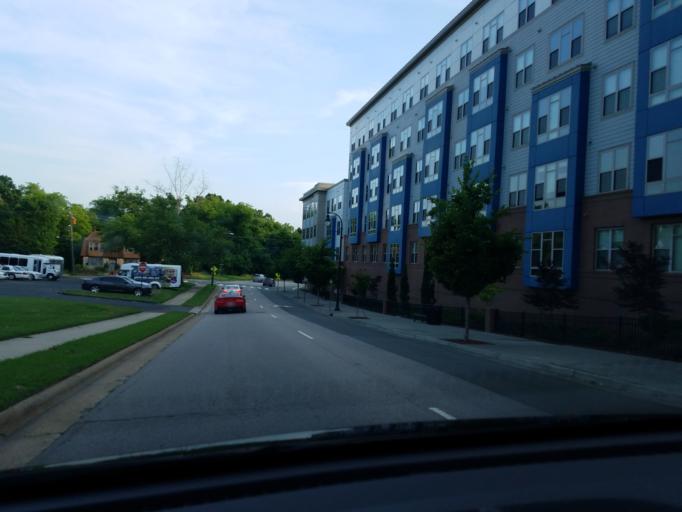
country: US
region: North Carolina
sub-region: Durham County
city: Durham
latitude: 35.9963
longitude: -78.9102
